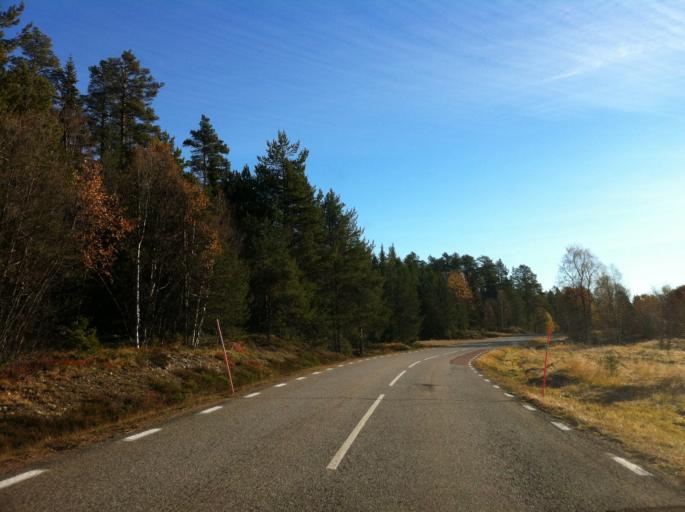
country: NO
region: Hedmark
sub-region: Engerdal
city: Engerdal
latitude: 62.0001
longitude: 12.4512
